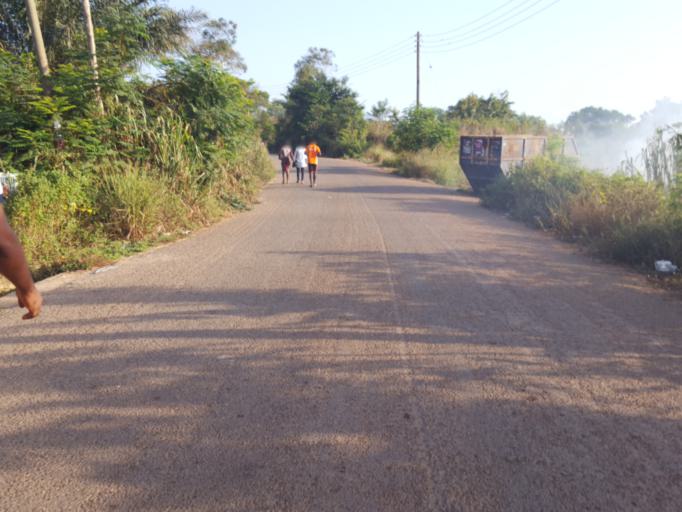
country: GH
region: Central
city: Cape Coast
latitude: 5.1127
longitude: -1.2914
